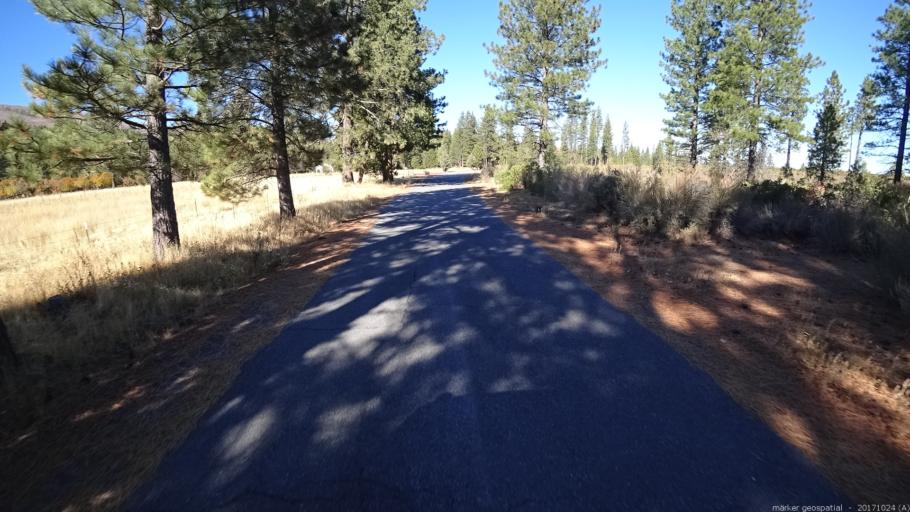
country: US
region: California
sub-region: Shasta County
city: Burney
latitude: 40.7516
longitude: -121.4774
